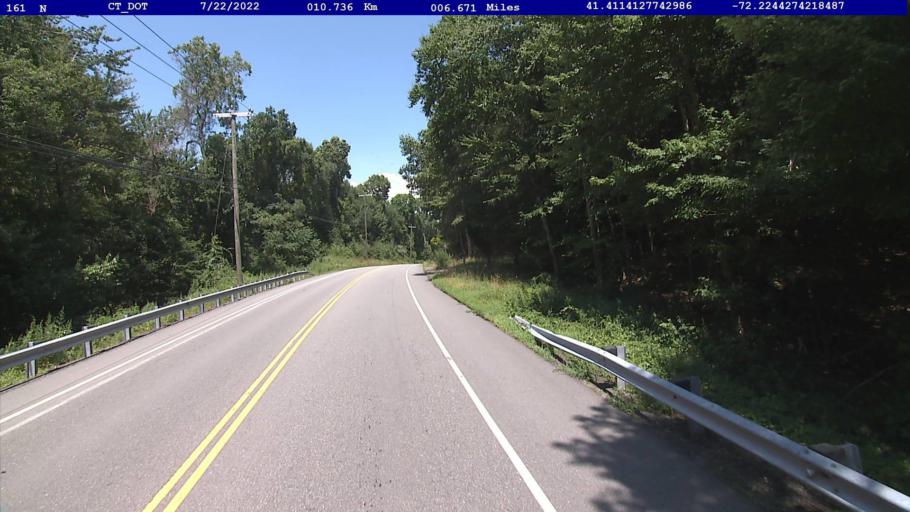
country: US
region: Connecticut
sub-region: New London County
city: Niantic
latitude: 41.4109
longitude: -72.2243
